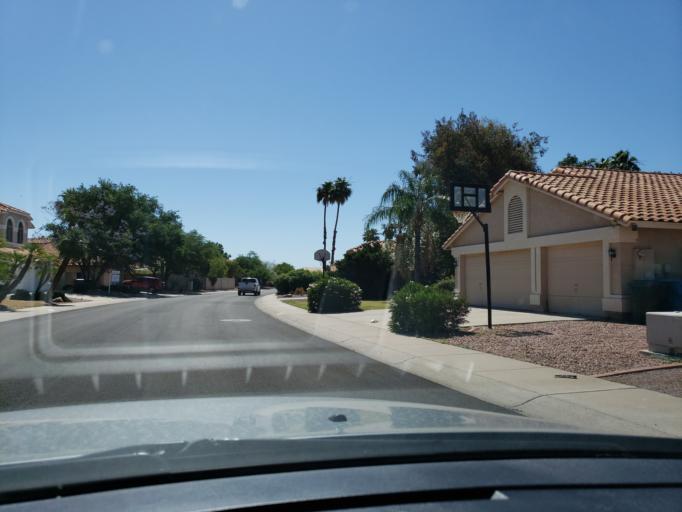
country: US
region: Arizona
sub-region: Maricopa County
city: Paradise Valley
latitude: 33.6180
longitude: -111.9596
